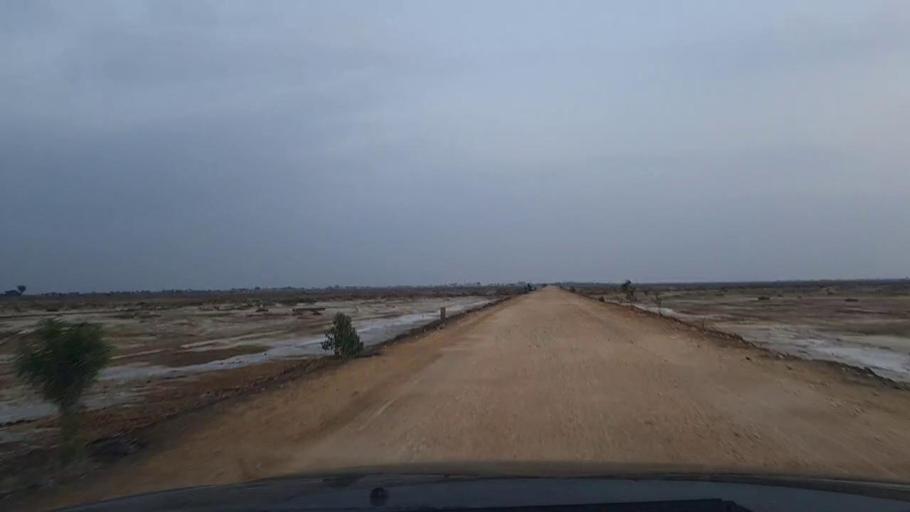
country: PK
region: Sindh
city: Jati
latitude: 24.4998
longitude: 68.3820
